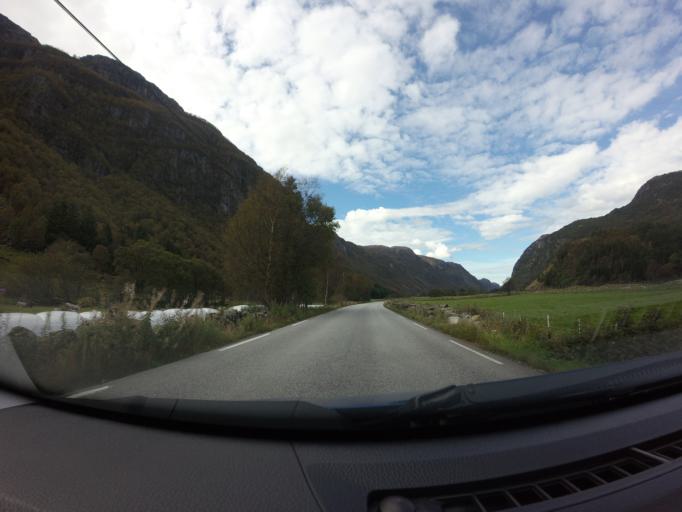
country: NO
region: Rogaland
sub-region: Forsand
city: Forsand
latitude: 58.8079
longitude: 6.2413
